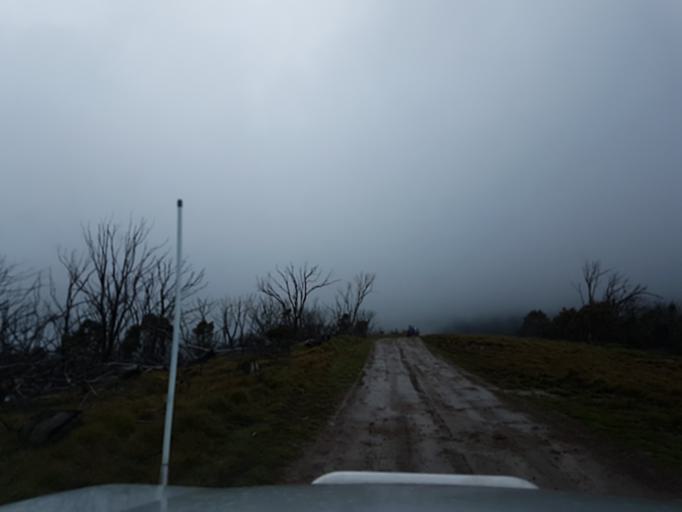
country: AU
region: Victoria
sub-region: Alpine
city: Mount Beauty
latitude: -37.0869
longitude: 147.1054
